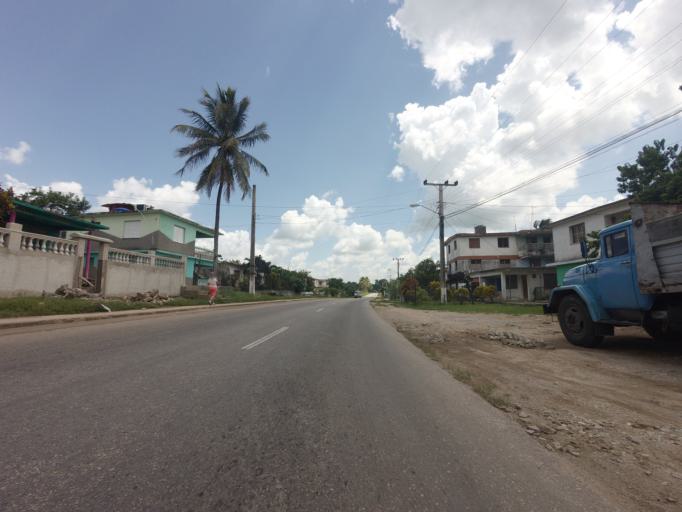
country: CU
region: La Habana
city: Arroyo Naranjo
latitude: 23.0007
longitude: -82.2979
